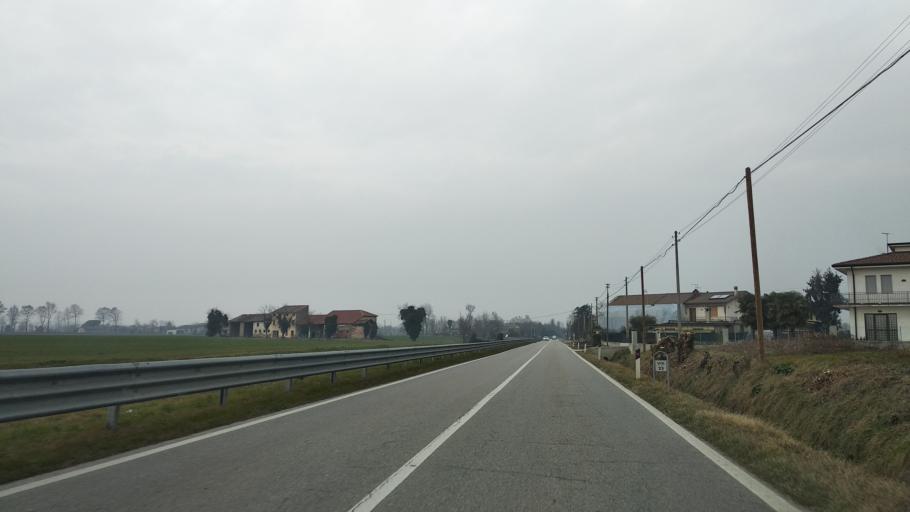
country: IT
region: Veneto
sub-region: Provincia di Padova
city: Villa del Conte
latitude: 45.5690
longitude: 11.8649
